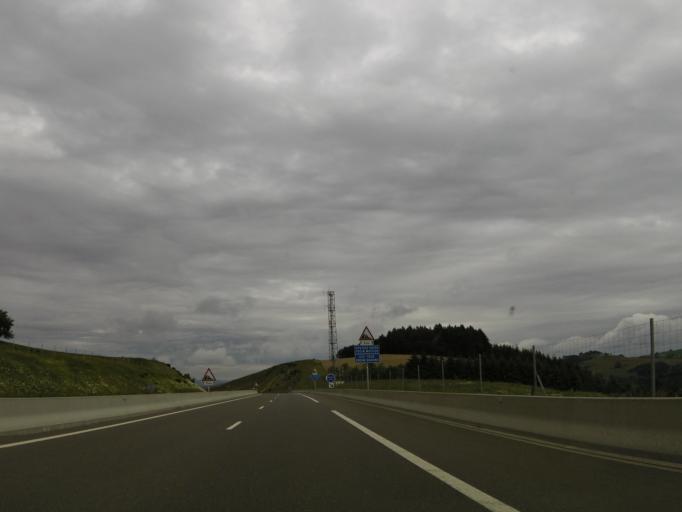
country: FR
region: Rhone-Alpes
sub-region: Departement de la Loire
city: Bussieres
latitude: 45.8684
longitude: 4.3009
